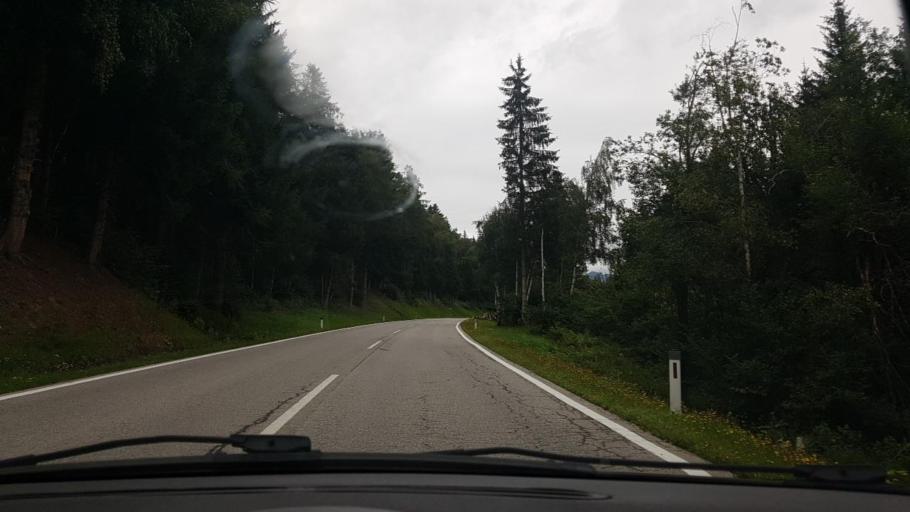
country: AT
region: Tyrol
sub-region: Politischer Bezirk Lienz
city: Dolsach
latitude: 46.8478
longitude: 12.8527
